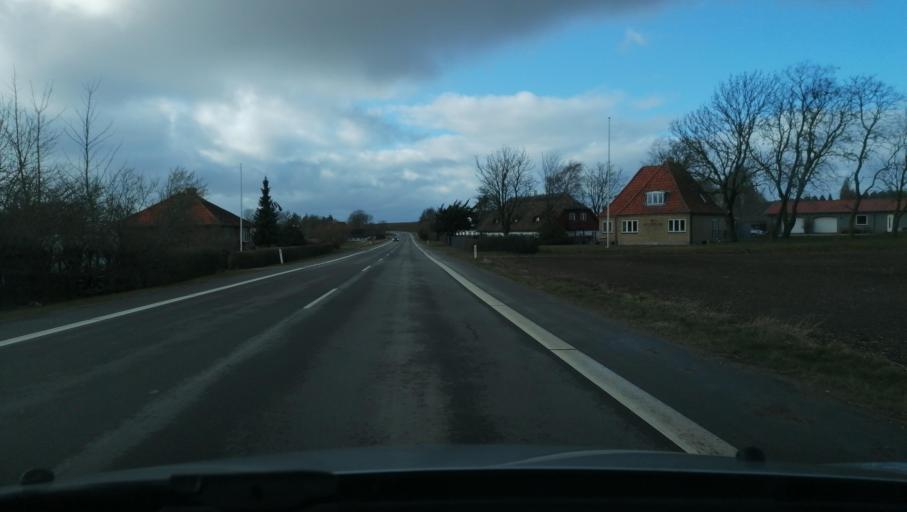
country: DK
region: Zealand
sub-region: Odsherred Kommune
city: Horve
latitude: 55.7610
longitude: 11.4429
